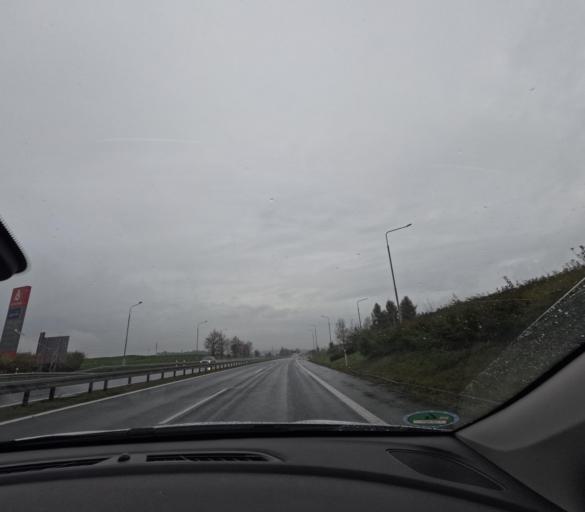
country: CZ
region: Central Bohemia
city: Velka Dobra
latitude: 50.1053
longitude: 14.0698
